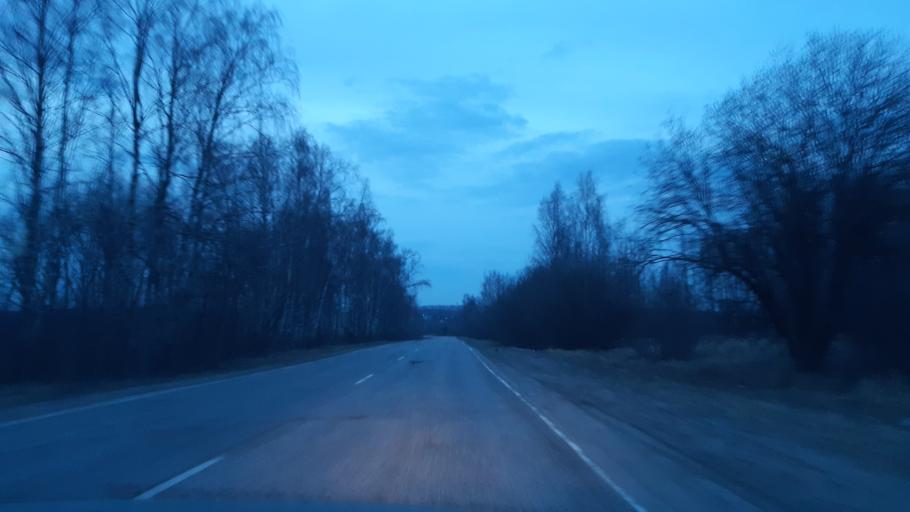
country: RU
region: Vladimir
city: Luknovo
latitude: 56.2055
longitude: 42.0330
